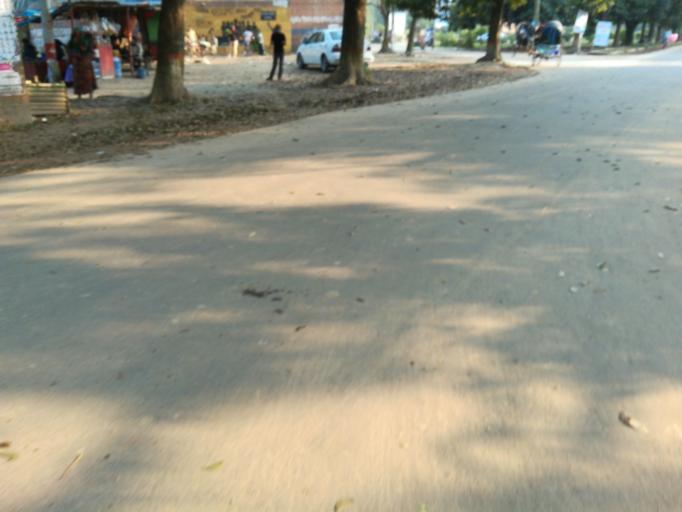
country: BD
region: Dhaka
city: Tungi
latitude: 23.8810
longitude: 90.2677
